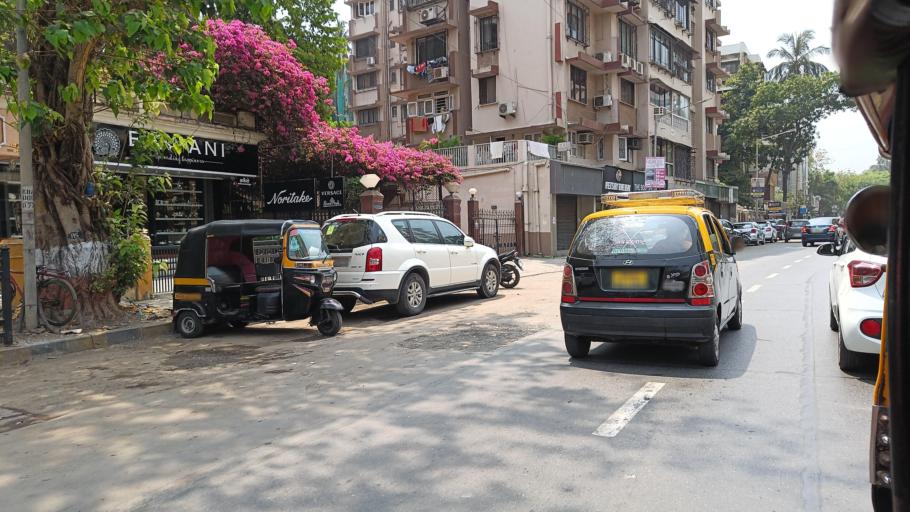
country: IN
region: Maharashtra
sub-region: Mumbai Suburban
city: Mumbai
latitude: 19.0908
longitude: 72.8276
